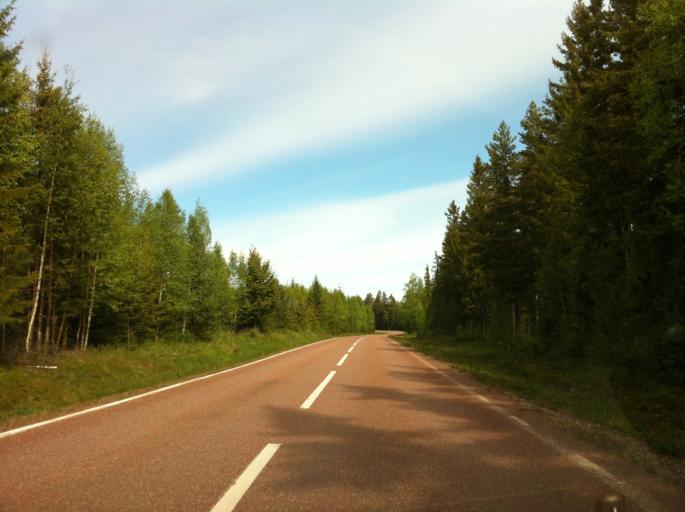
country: SE
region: Dalarna
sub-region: Mora Kommun
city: Mora
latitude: 60.8483
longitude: 14.6385
